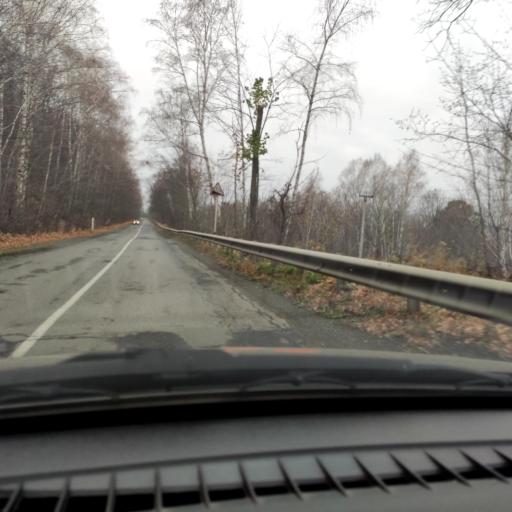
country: RU
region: Samara
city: Povolzhskiy
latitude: 53.4387
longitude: 49.6915
